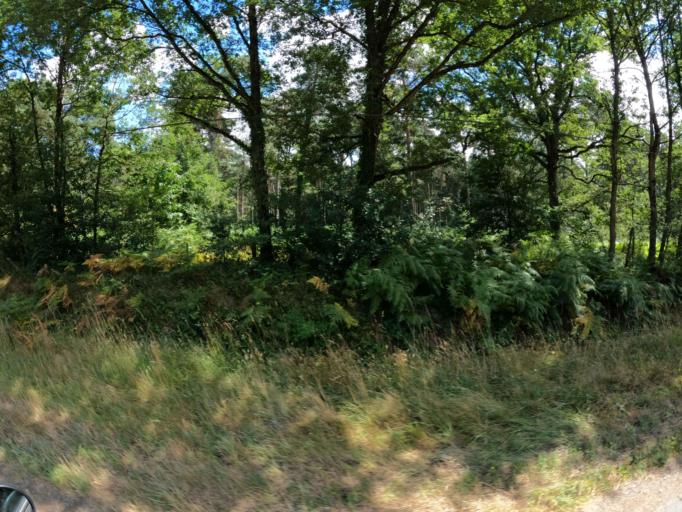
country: FR
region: Pays de la Loire
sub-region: Departement de la Sarthe
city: Juigne-sur-Sarthe
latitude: 47.9018
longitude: -0.2812
